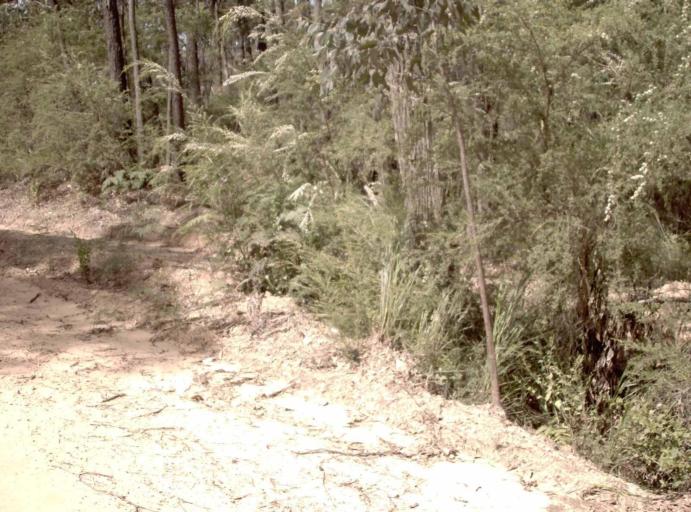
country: AU
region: Victoria
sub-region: East Gippsland
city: Lakes Entrance
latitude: -37.6662
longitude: 148.6328
